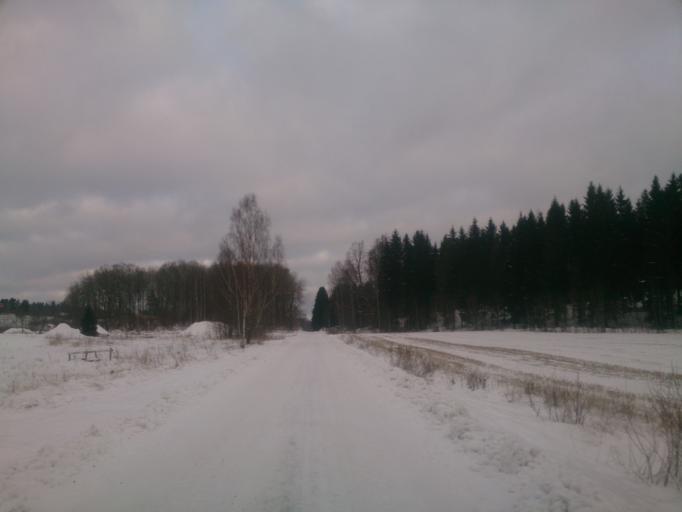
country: SE
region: OEstergoetland
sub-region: Atvidabergs Kommun
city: Atvidaberg
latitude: 58.2166
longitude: 15.9893
